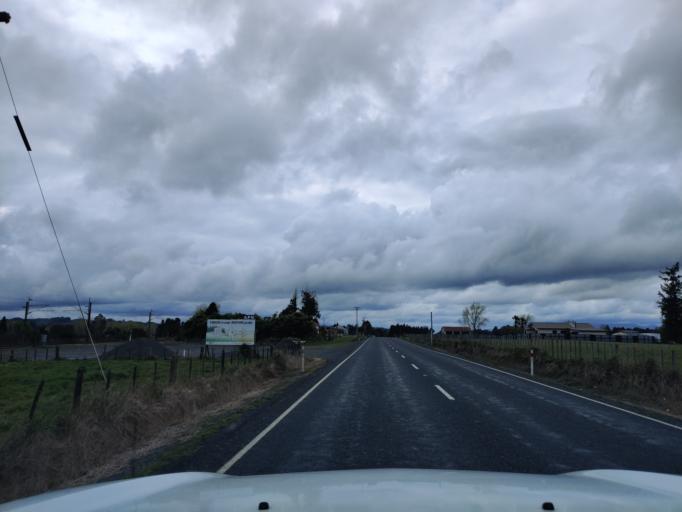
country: NZ
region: Waikato
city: Turangi
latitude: -39.0080
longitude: 175.3773
